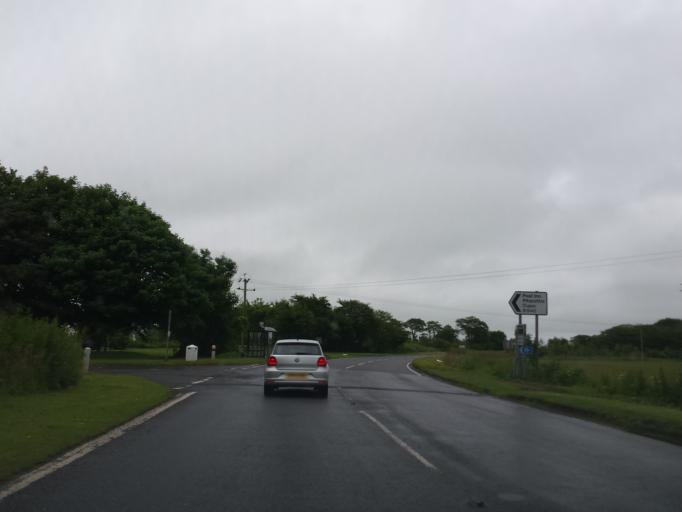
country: GB
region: Scotland
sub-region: Fife
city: Strathkinness
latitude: 56.2741
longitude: -2.8490
